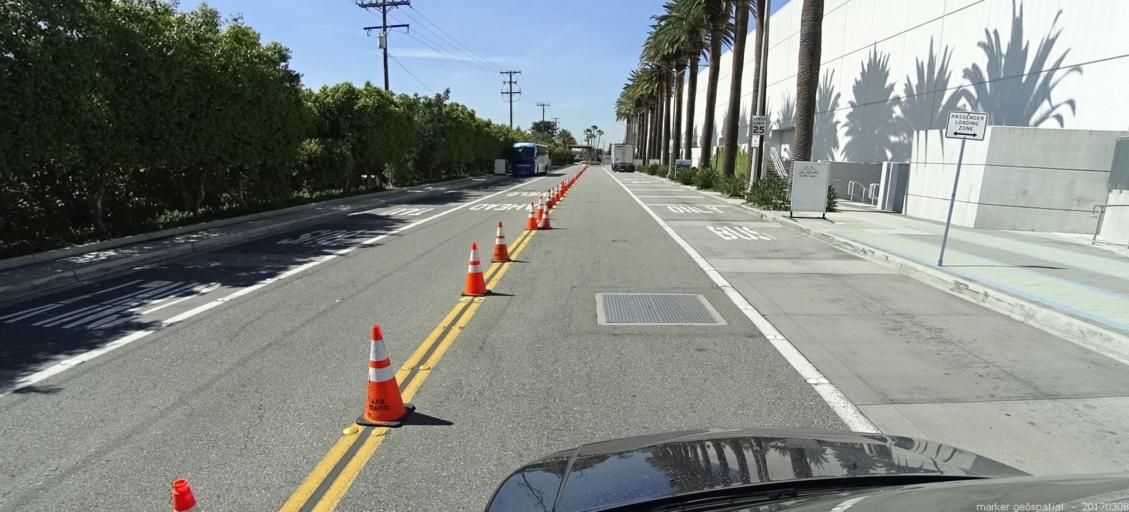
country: US
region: California
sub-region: Orange County
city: Garden Grove
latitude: 33.7980
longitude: -117.9210
